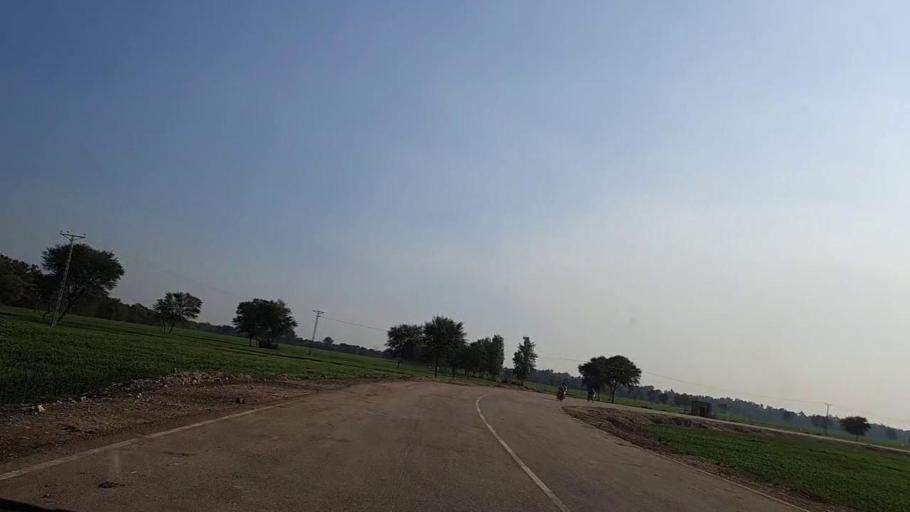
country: PK
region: Sindh
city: Sakrand
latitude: 26.1187
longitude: 68.2496
